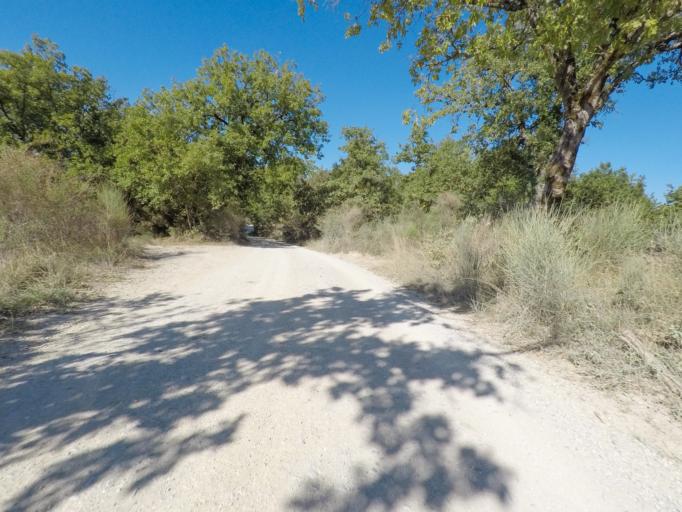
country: IT
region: Tuscany
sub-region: Provincia di Siena
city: Castellina in Chianti
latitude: 43.4345
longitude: 11.3324
